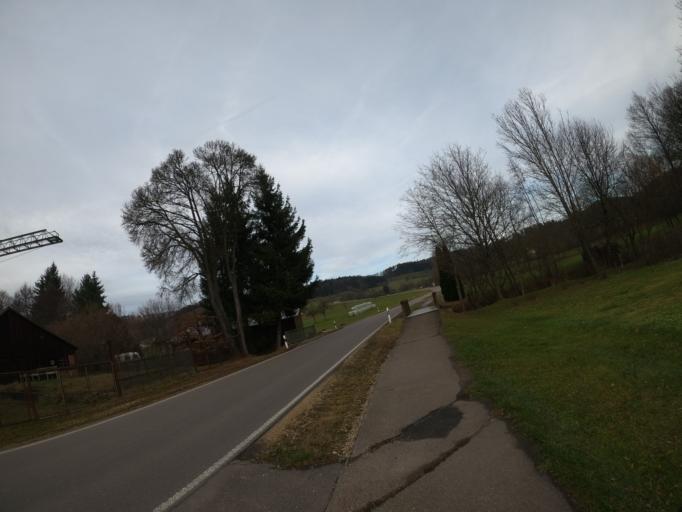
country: DE
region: Baden-Wuerttemberg
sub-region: Regierungsbezirk Stuttgart
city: Ottenbach
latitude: 48.7401
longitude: 9.7510
